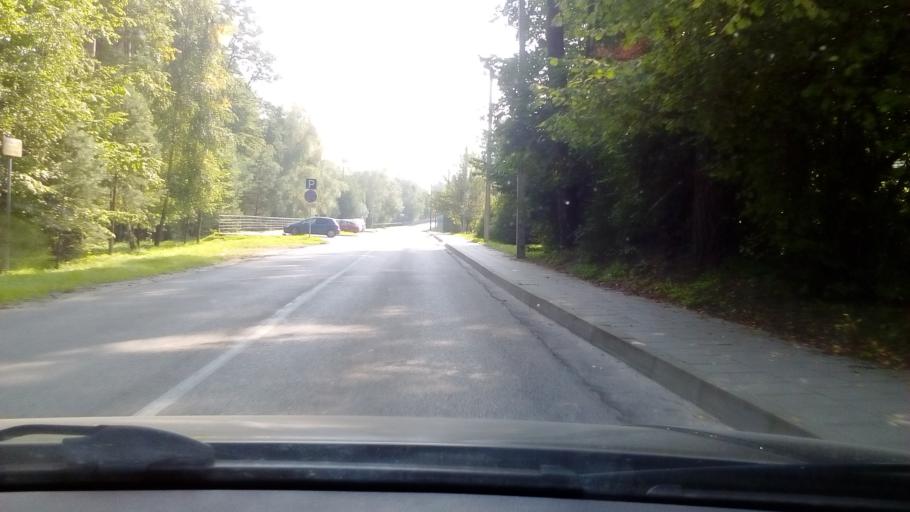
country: LT
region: Alytaus apskritis
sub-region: Alytus
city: Alytus
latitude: 54.3911
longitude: 24.0601
